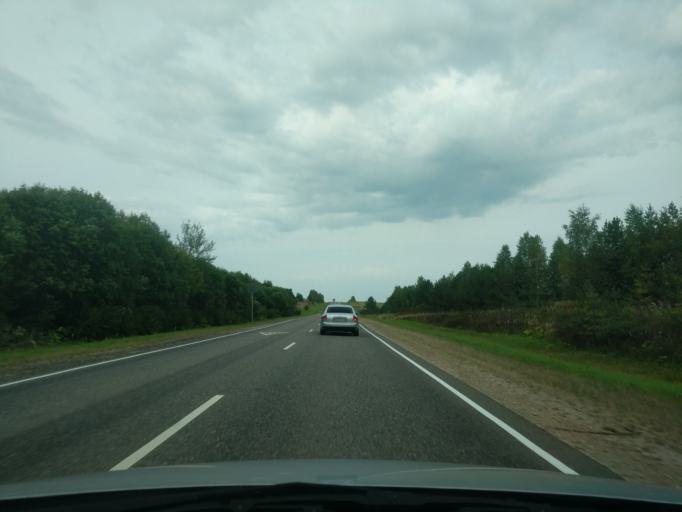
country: RU
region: Kirov
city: Mirnyy
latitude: 58.2729
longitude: 47.7817
